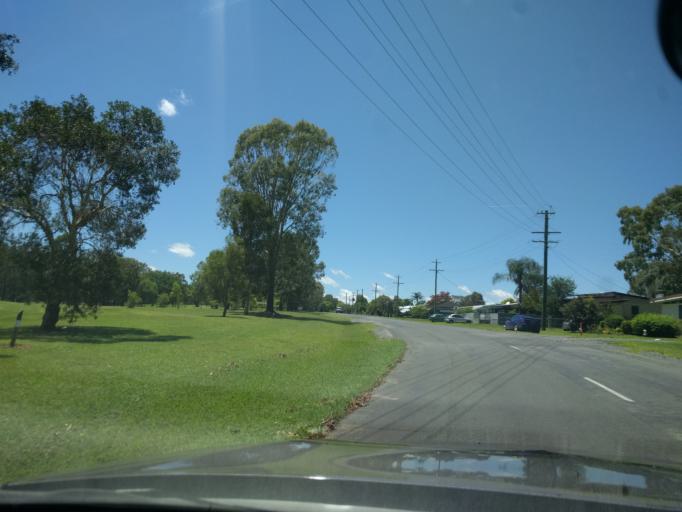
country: AU
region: Queensland
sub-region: Logan
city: Cedar Vale
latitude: -27.9968
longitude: 152.9981
